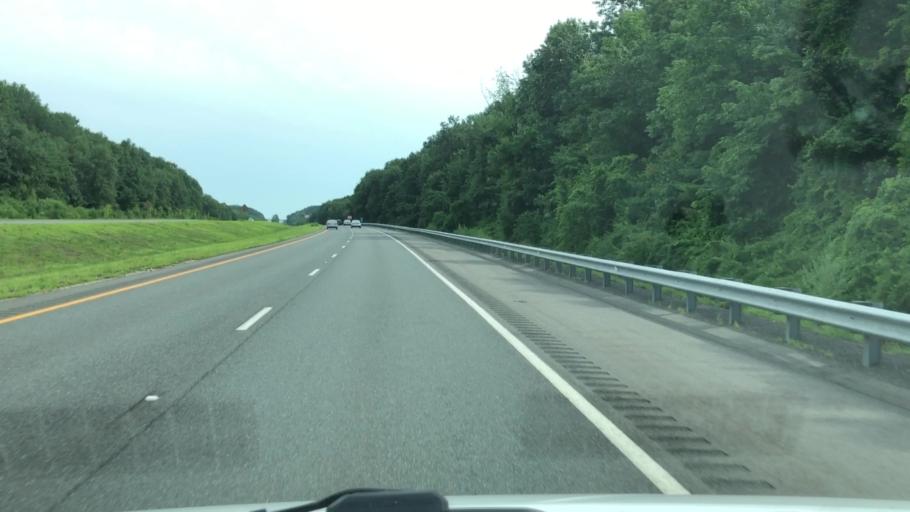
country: US
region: Massachusetts
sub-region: Franklin County
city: South Deerfield
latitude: 42.5304
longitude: -72.6282
